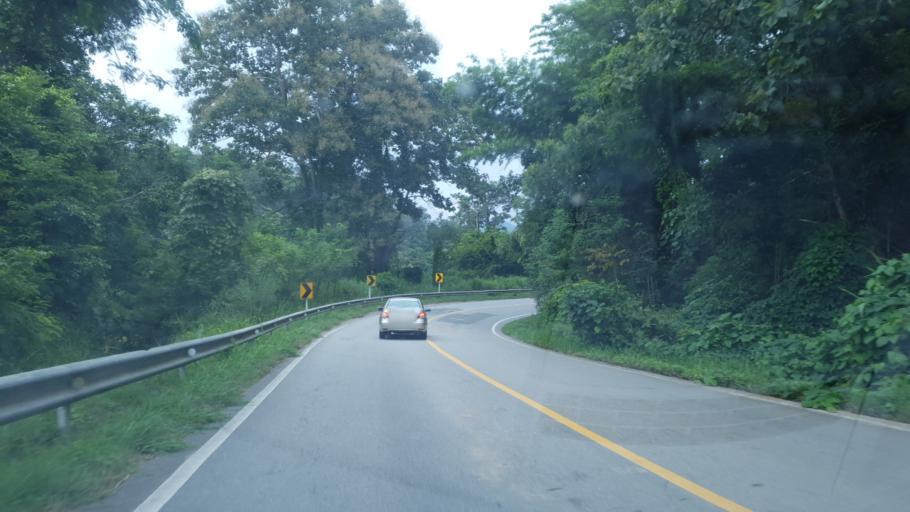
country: TH
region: Mae Hong Son
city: Khun Yuam
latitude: 18.7085
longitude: 97.9112
